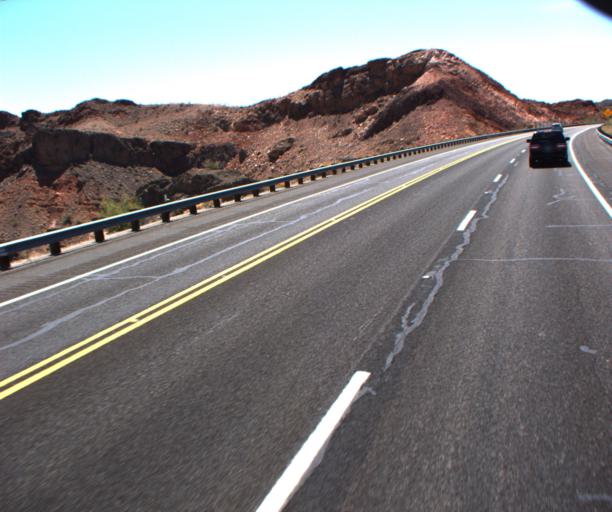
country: US
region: Arizona
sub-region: La Paz County
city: Cienega Springs
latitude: 34.2475
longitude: -114.1637
